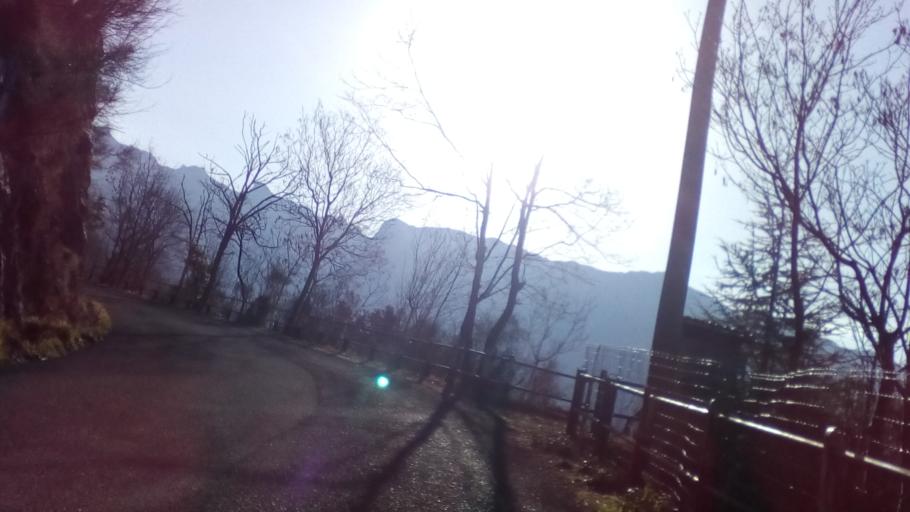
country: IT
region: Tuscany
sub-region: Provincia di Massa-Carrara
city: Montignoso
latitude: 44.0577
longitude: 10.1890
